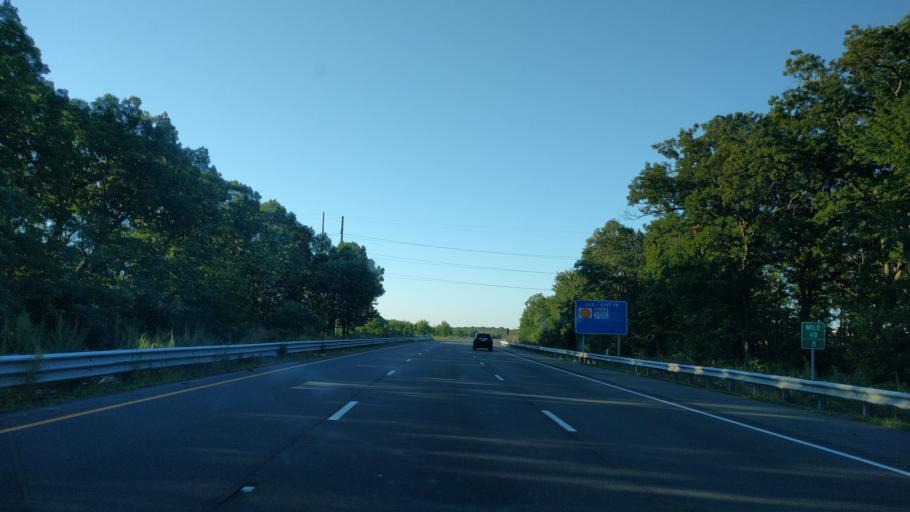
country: US
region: Massachusetts
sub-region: Worcester County
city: Milford
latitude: 42.1541
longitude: -71.4878
